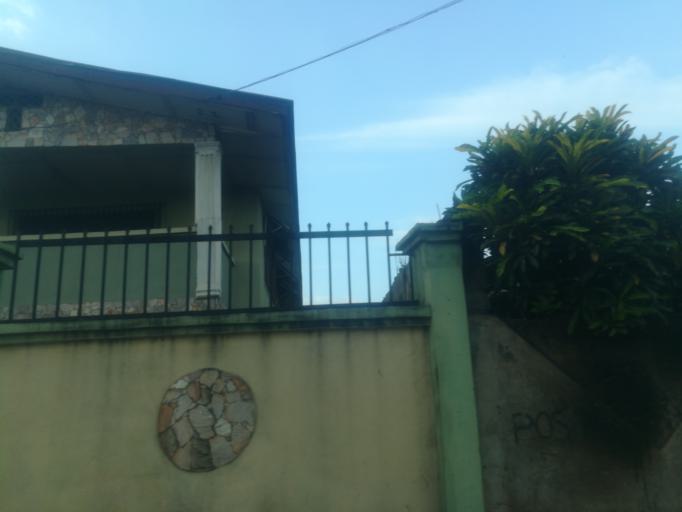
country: NG
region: Oyo
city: Ibadan
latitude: 7.4079
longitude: 3.9483
